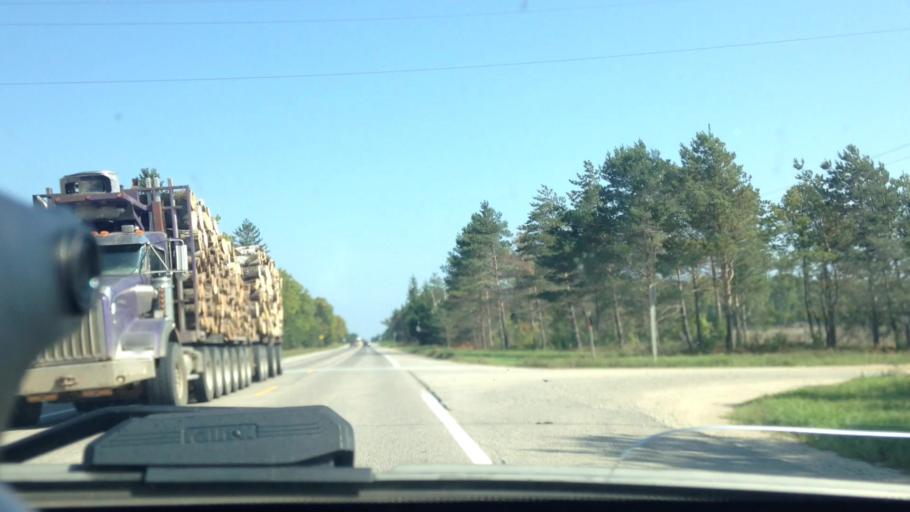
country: US
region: Michigan
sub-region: Luce County
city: Newberry
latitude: 46.3034
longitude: -85.4682
